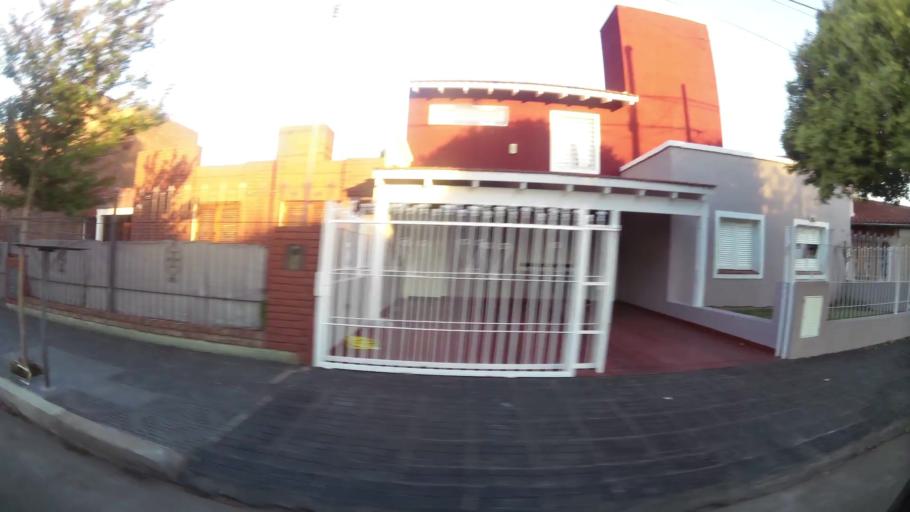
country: AR
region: Cordoba
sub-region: Departamento de Capital
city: Cordoba
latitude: -31.3768
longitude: -64.2171
